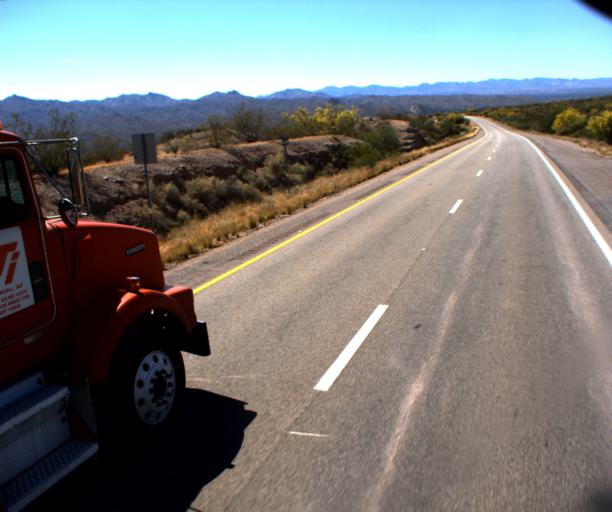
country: US
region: Arizona
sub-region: Yavapai County
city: Bagdad
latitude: 34.6249
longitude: -113.5351
